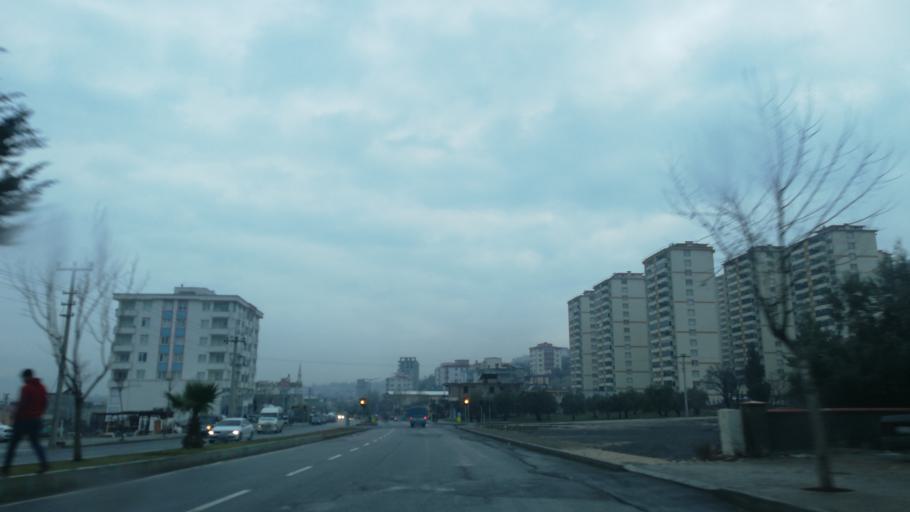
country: TR
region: Kahramanmaras
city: Kahramanmaras
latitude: 37.5819
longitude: 36.9663
